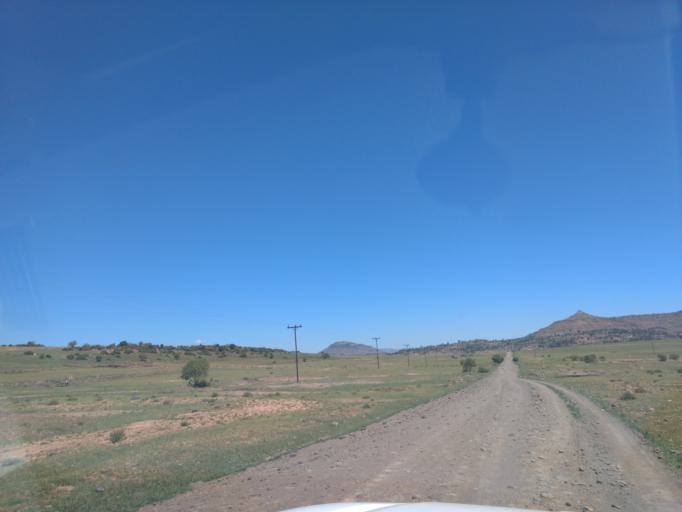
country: LS
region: Maseru
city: Maseru
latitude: -29.4695
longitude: 27.3757
